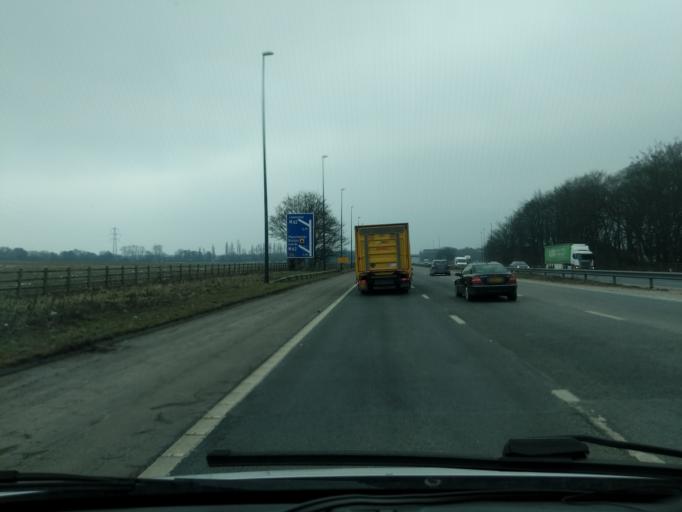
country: GB
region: England
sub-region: Warrington
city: Croft
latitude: 53.4340
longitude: -2.5707
